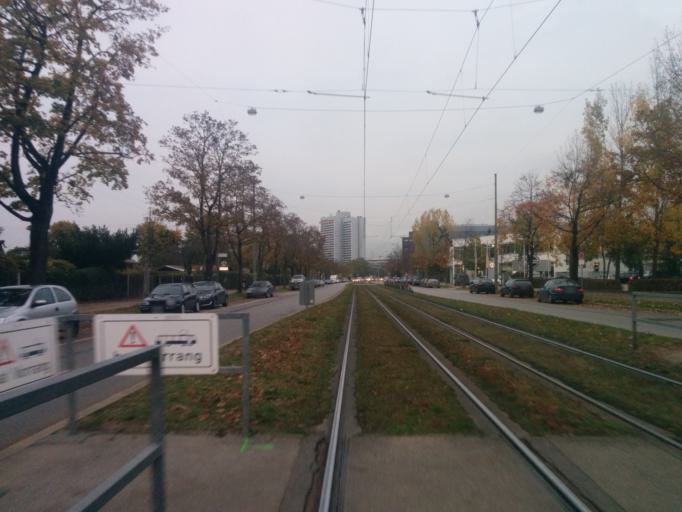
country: DE
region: Bavaria
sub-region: Upper Bavaria
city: Munich
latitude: 48.1304
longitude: 11.5177
